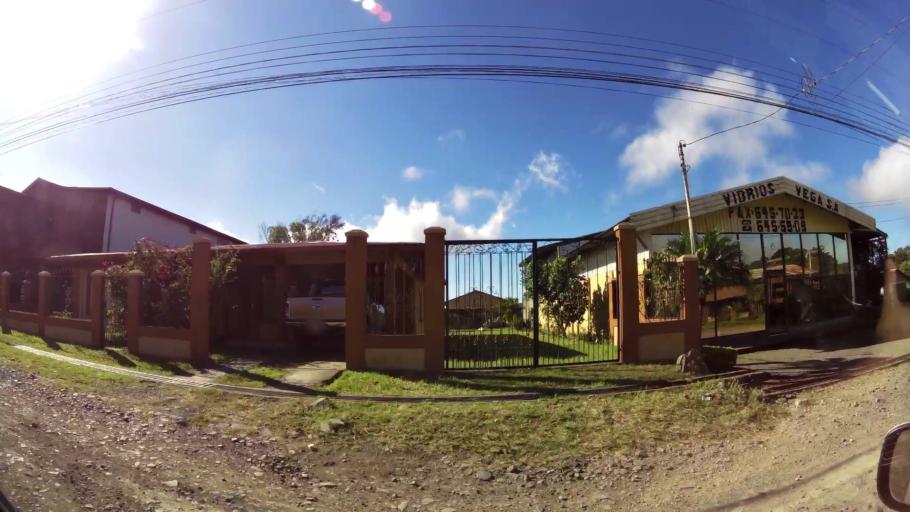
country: CR
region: Guanacaste
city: Juntas
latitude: 10.3148
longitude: -84.8281
